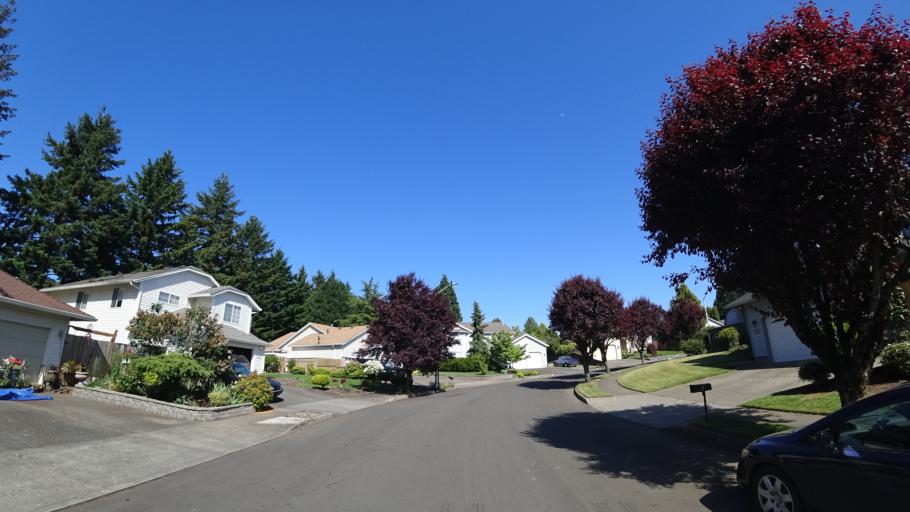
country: US
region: Oregon
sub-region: Multnomah County
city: Gresham
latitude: 45.4955
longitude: -122.4734
